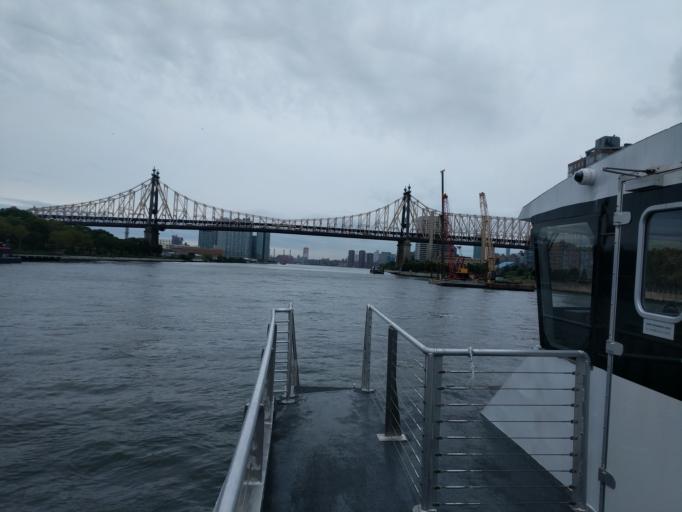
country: US
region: New York
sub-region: Queens County
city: Long Island City
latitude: 40.7605
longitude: -73.9482
